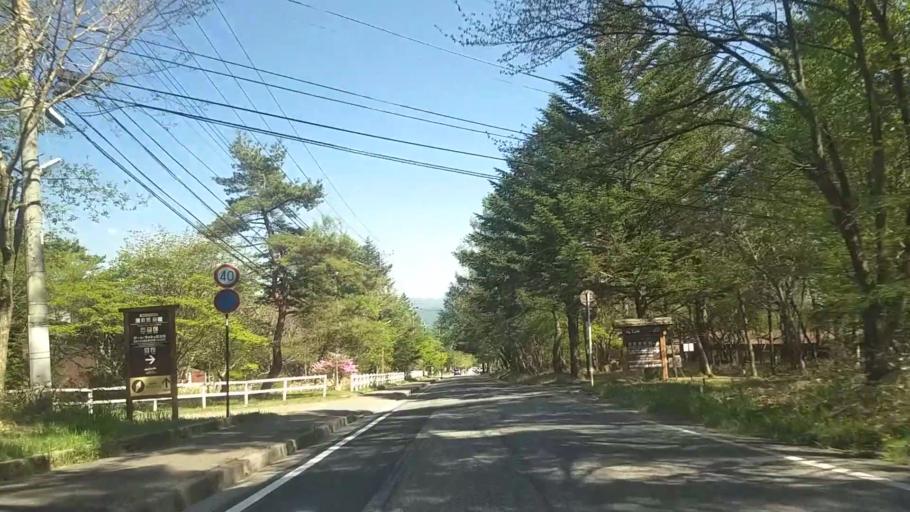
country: JP
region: Yamanashi
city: Nirasaki
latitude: 35.9269
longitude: 138.4191
